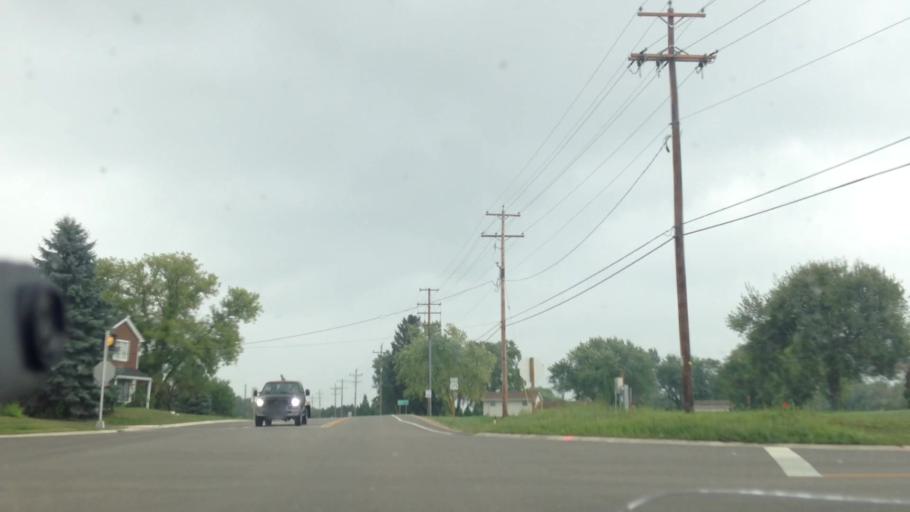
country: US
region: Wisconsin
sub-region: Washington County
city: Richfield
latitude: 43.2811
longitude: -88.2117
